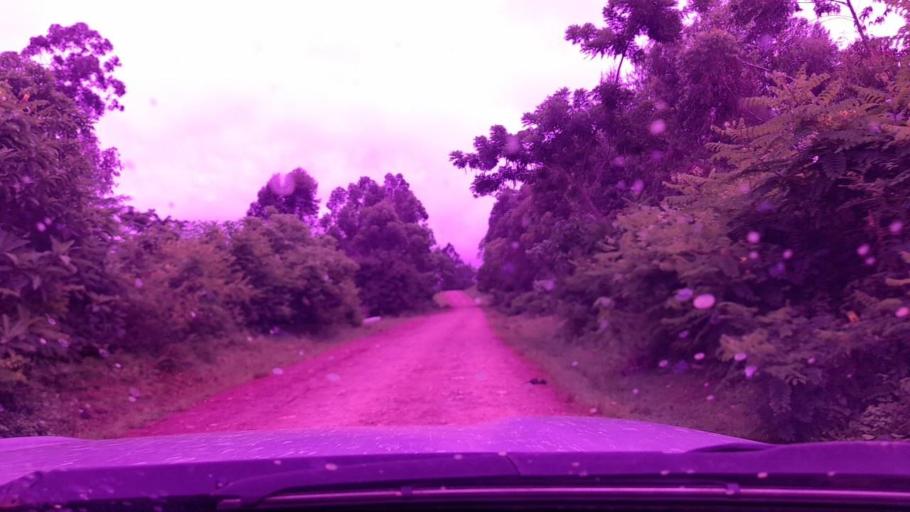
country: ET
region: Southern Nations, Nationalities, and People's Region
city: Bonga
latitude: 7.5470
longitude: 35.8472
